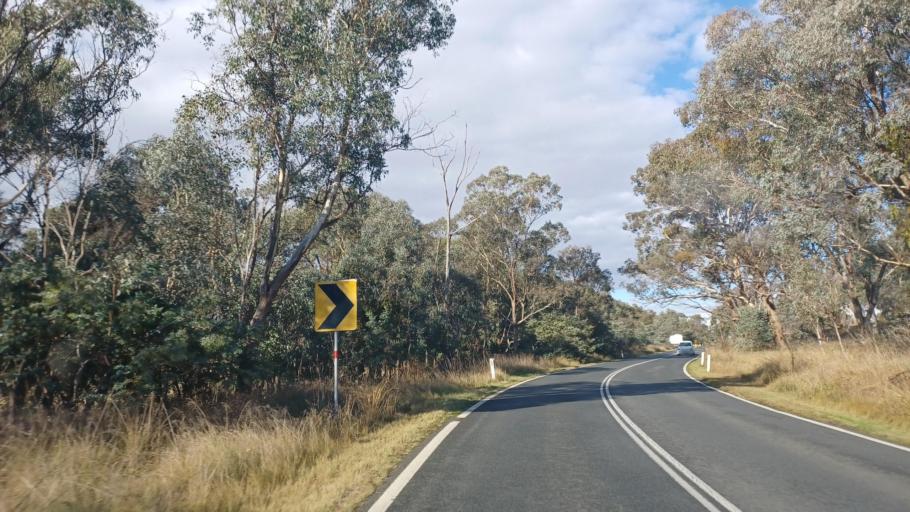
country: AU
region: Australian Capital Territory
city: Belconnen
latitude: -35.1890
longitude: 149.0572
